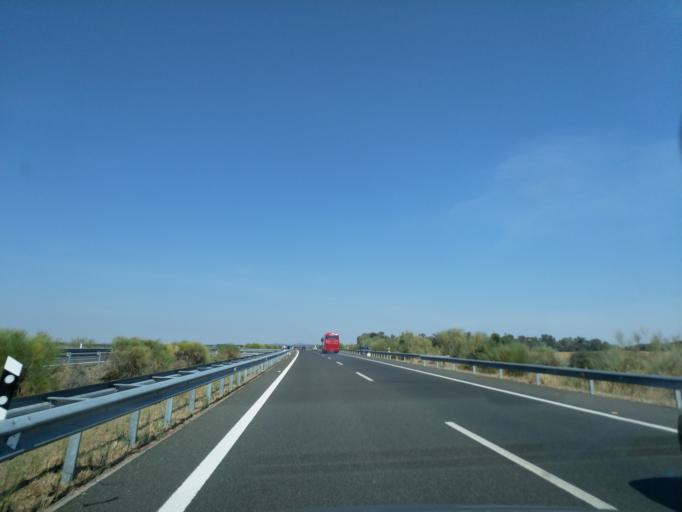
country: ES
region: Extremadura
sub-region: Provincia de Caceres
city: Casas de Don Antonio
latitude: 39.2453
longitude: -6.3057
